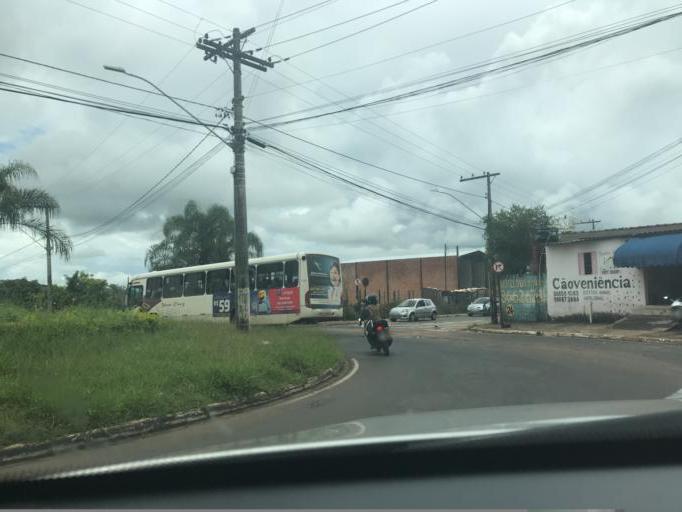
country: BR
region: Minas Gerais
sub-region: Araxa
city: Araxa
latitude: -19.5808
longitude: -46.9357
